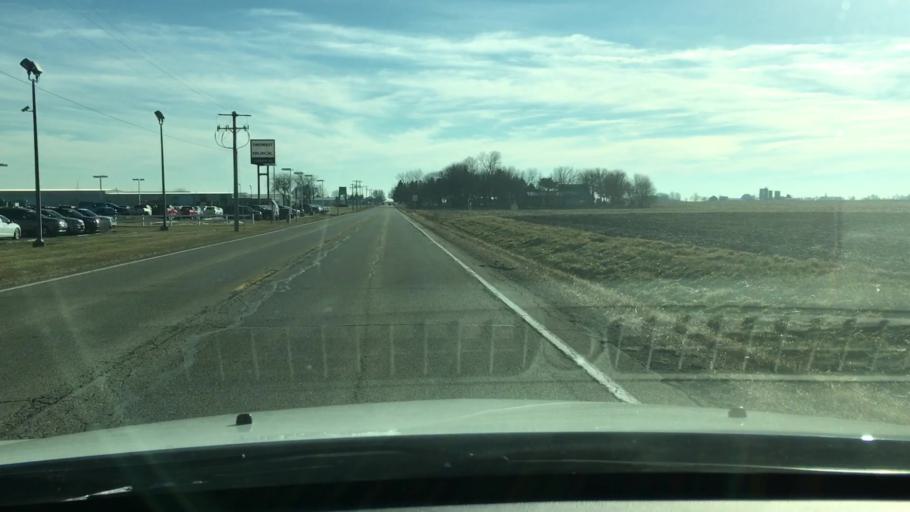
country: US
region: Illinois
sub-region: LaSalle County
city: Mendota
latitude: 41.5261
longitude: -89.1275
